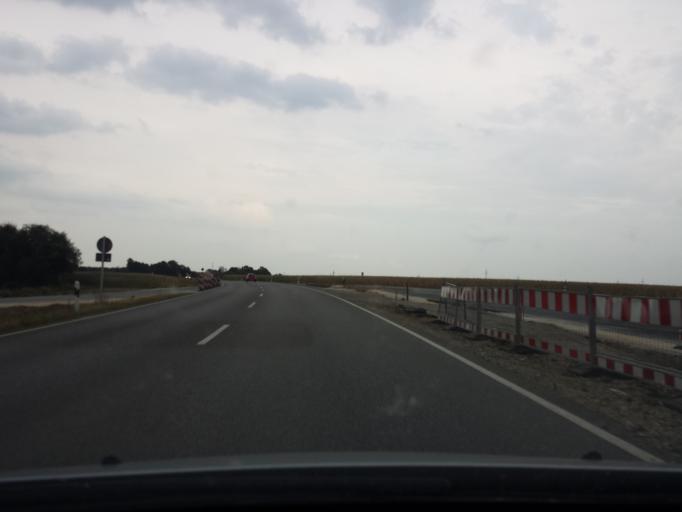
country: DE
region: Bavaria
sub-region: Swabia
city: Nersingen
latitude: 48.4166
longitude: 10.1028
